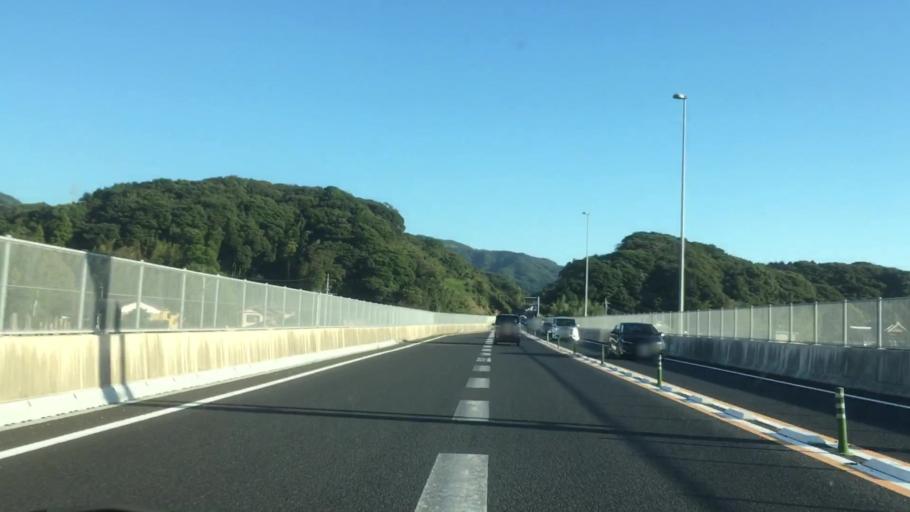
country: JP
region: Nagasaki
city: Sasebo
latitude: 33.2008
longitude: 129.6741
